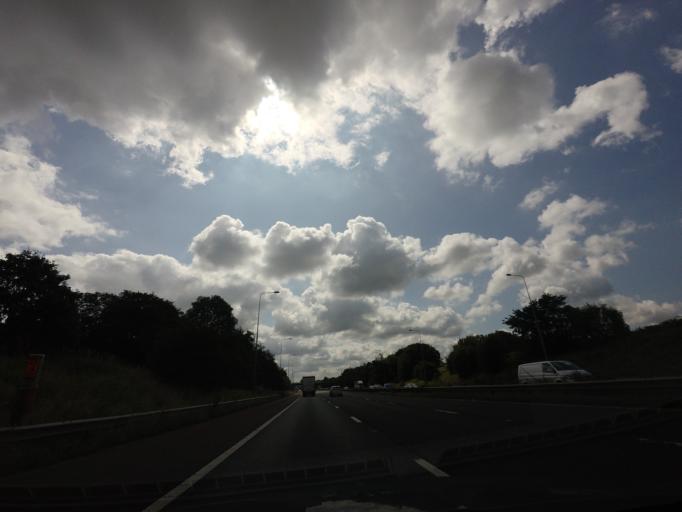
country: GB
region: England
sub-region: Lancashire
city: Coppull
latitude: 53.6372
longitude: -2.6920
